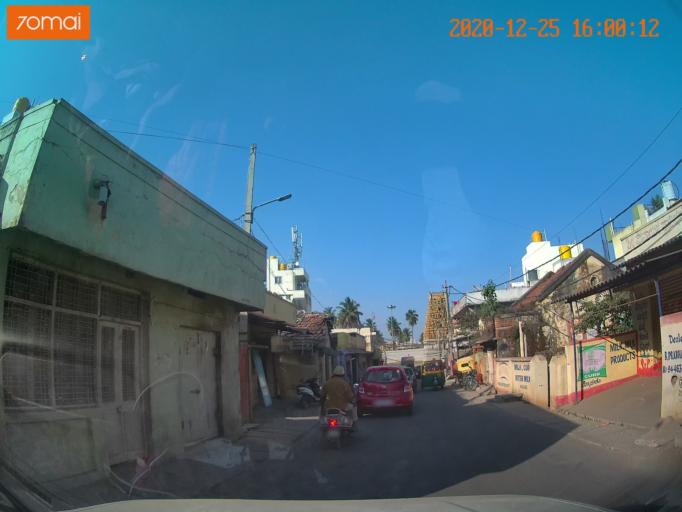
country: IN
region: Karnataka
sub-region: Bangalore Urban
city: Bangalore
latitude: 12.8755
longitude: 77.6261
